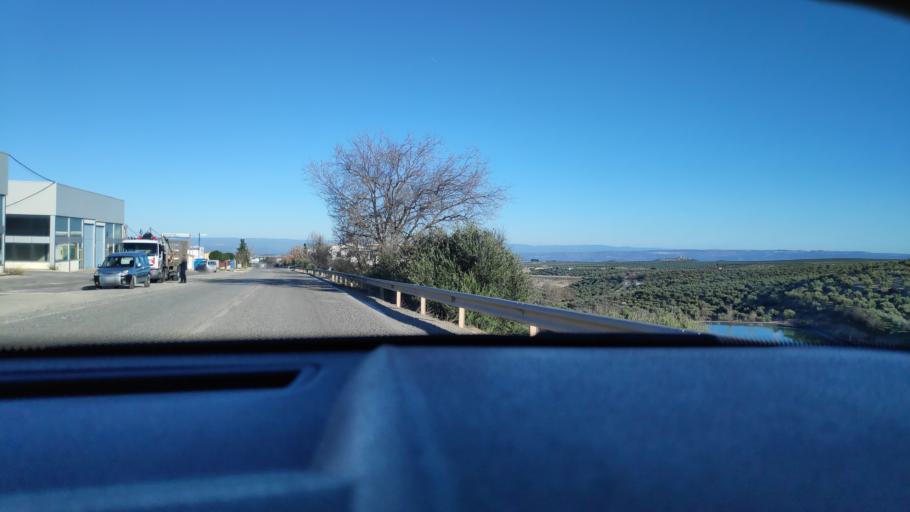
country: ES
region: Andalusia
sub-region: Provincia de Jaen
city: Mancha Real
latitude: 37.7998
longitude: -3.6095
